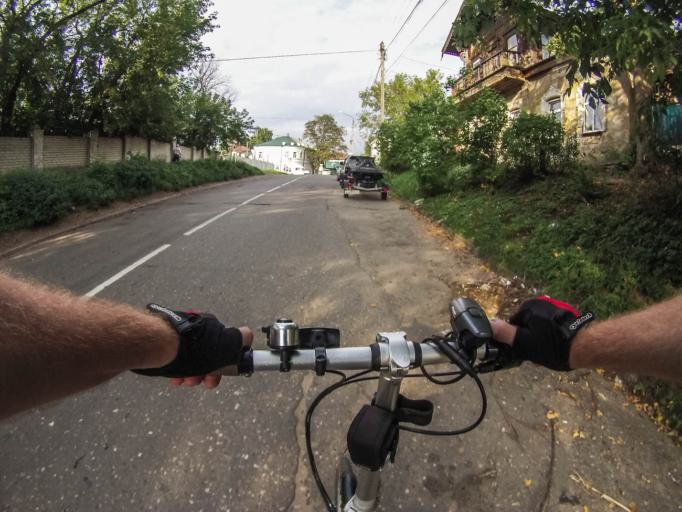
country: RU
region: Kostroma
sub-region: Kostromskoy Rayon
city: Kostroma
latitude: 57.7709
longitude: 40.9142
